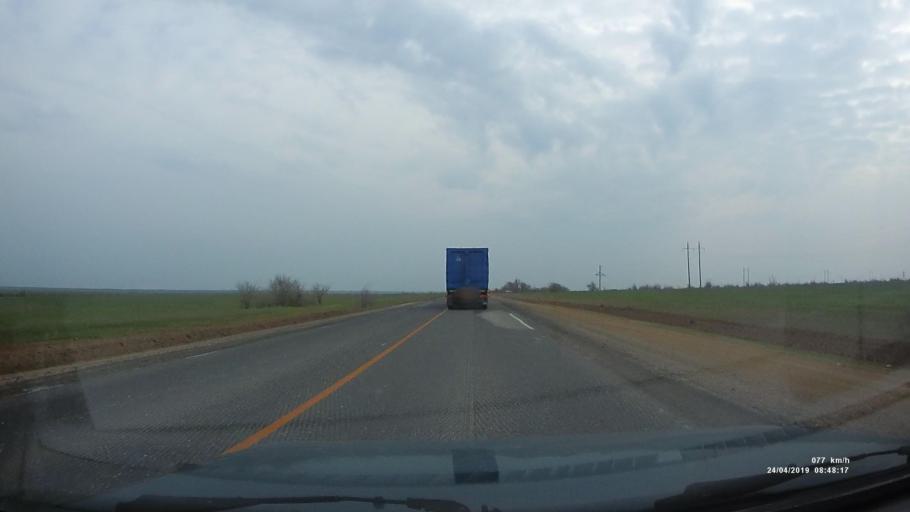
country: RU
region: Kalmykiya
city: Arshan'
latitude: 46.2501
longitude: 44.1066
